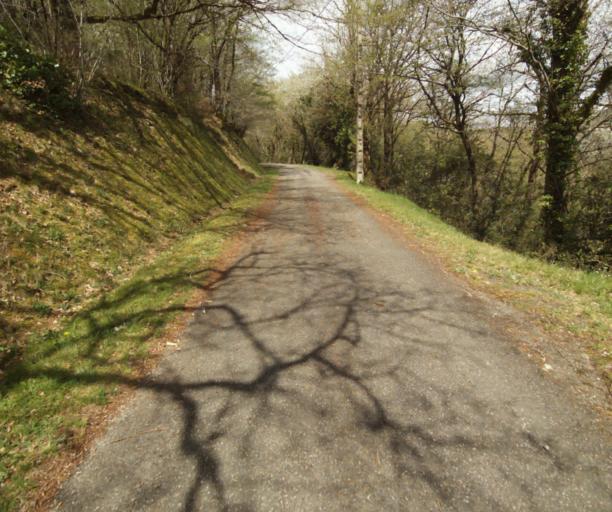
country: FR
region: Limousin
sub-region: Departement de la Correze
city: Sainte-Fortunade
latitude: 45.1771
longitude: 1.8715
